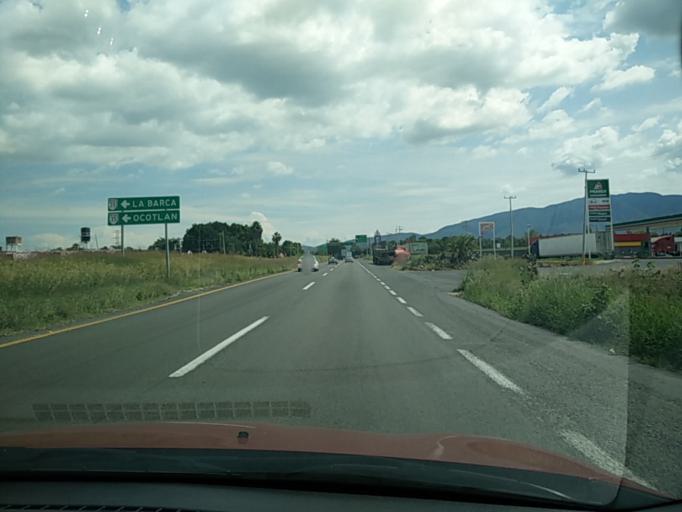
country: MX
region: Jalisco
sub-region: Ixtlahuacan de los Membrillos
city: Los Olivos
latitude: 20.4218
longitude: -103.2367
